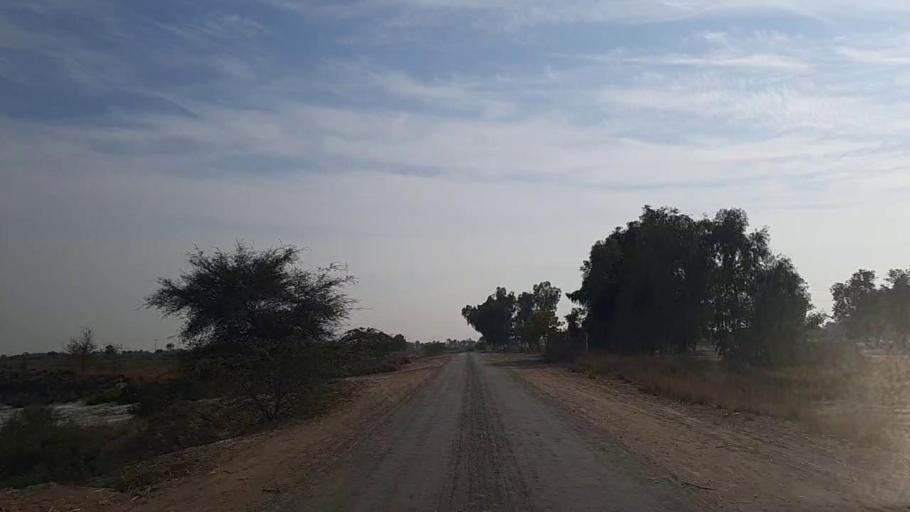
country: PK
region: Sindh
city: Daur
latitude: 26.4722
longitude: 68.4180
